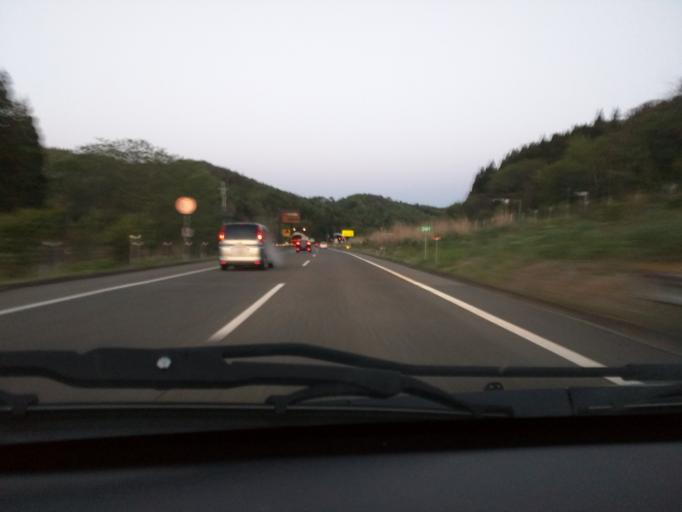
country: JP
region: Niigata
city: Kashiwazaki
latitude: 37.3389
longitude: 138.5326
